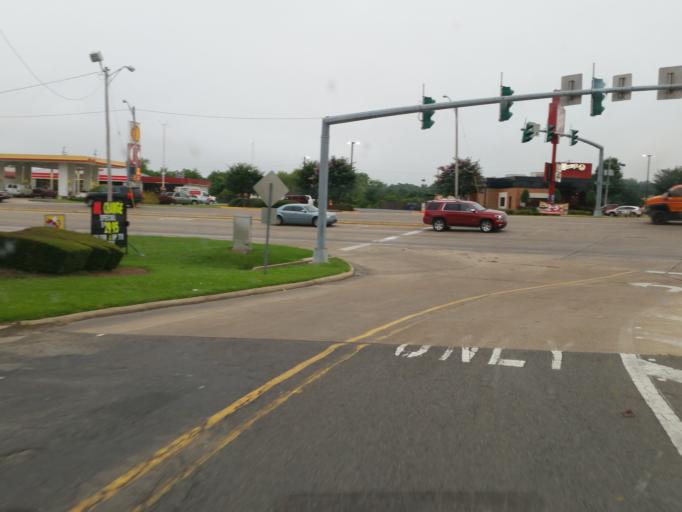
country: US
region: Louisiana
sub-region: Caddo Parish
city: Greenwood
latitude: 32.4484
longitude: -93.8650
